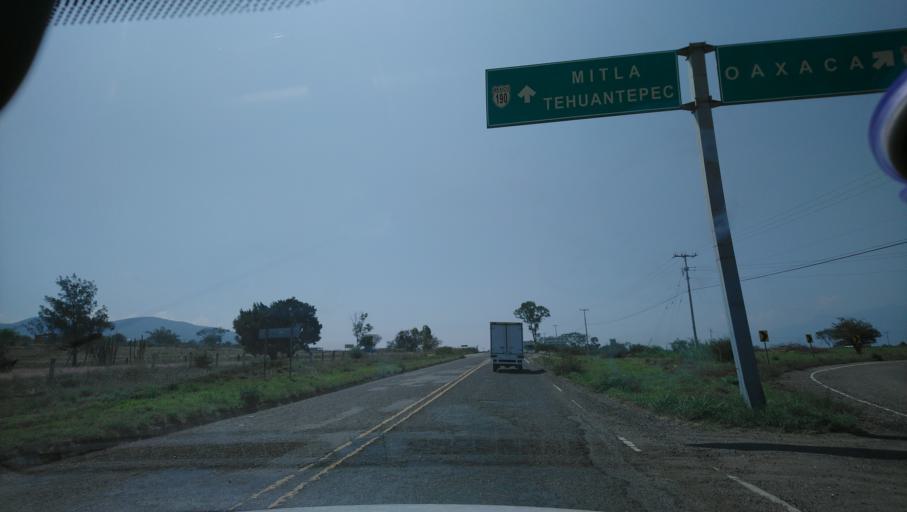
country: MX
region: Oaxaca
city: Santa Maria del Tule
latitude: 17.0388
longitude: -96.6203
